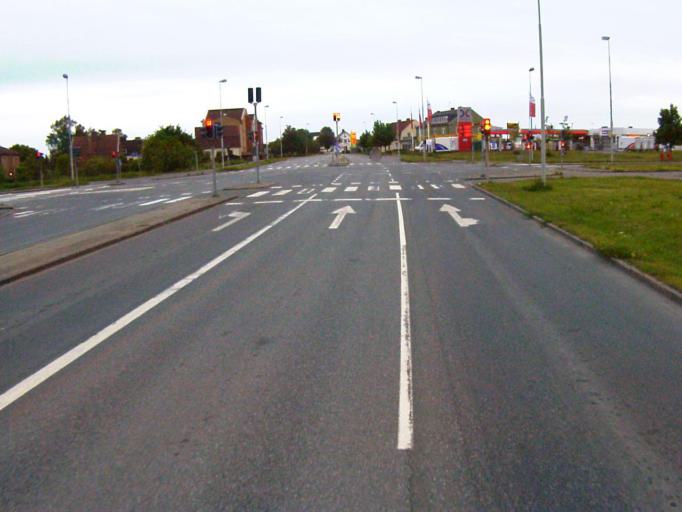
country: SE
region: Skane
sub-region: Kristianstads Kommun
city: Kristianstad
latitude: 56.0219
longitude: 14.1450
